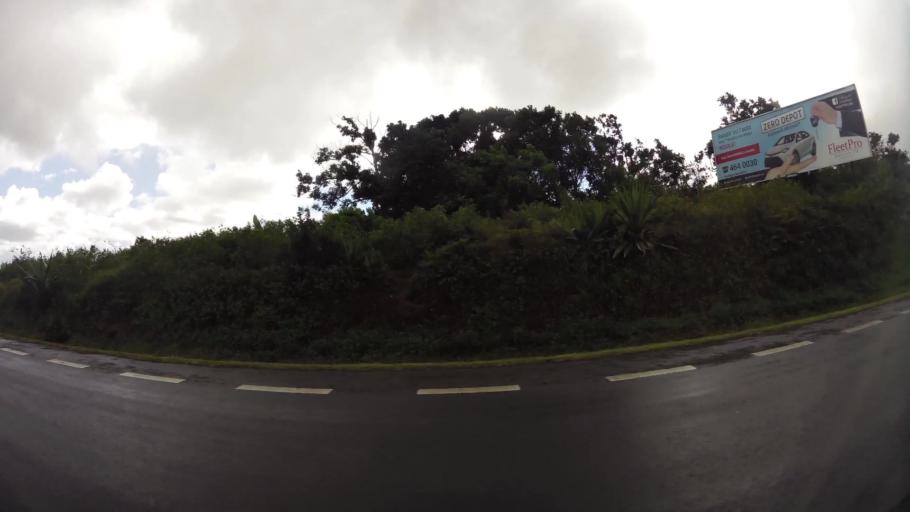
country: MU
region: Plaines Wilhems
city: Curepipe
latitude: -20.2843
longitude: 57.5198
